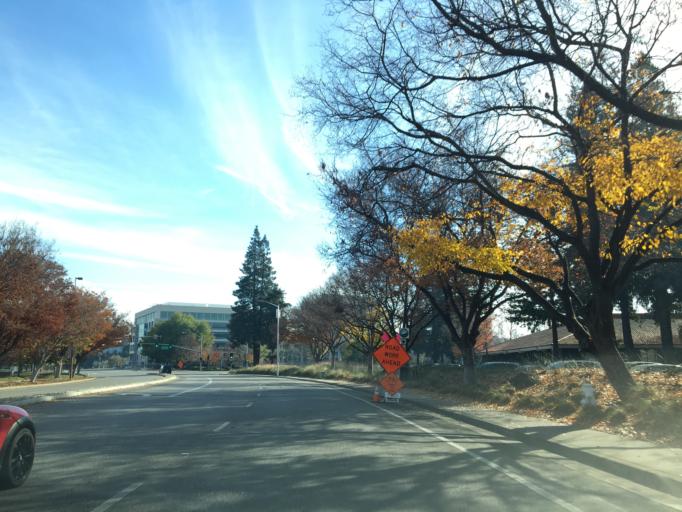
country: US
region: California
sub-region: Santa Clara County
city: Santa Clara
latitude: 37.3895
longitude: -121.9713
